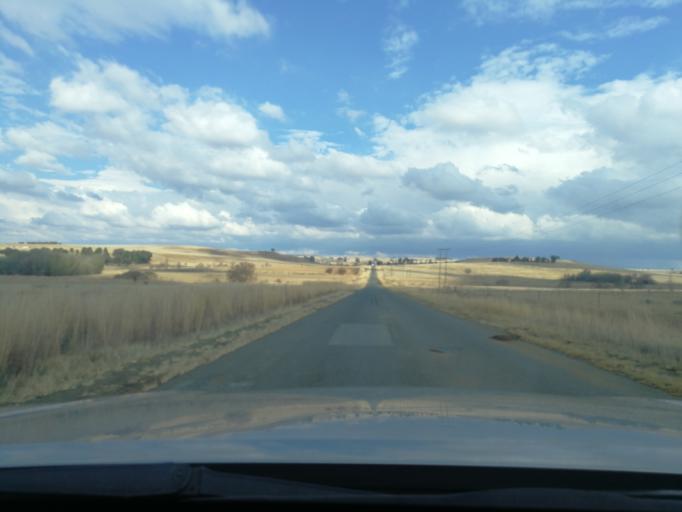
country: ZA
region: Orange Free State
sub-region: Fezile Dabi District Municipality
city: Frankfort
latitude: -27.4668
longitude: 28.5238
